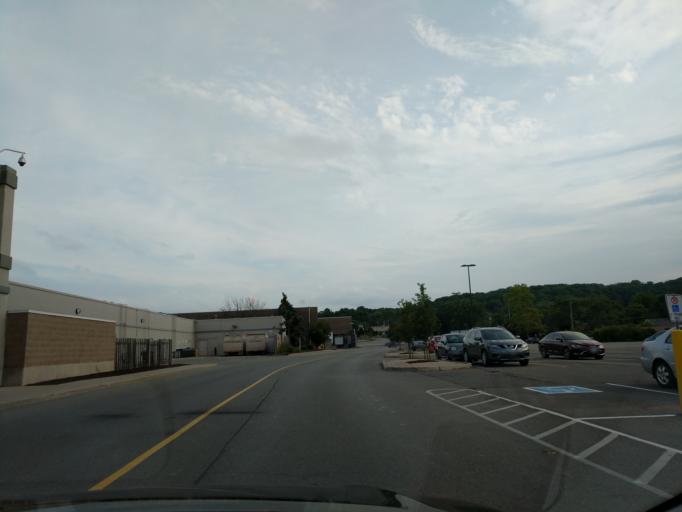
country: CA
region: Ontario
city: Thorold
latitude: 43.1354
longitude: -79.2263
